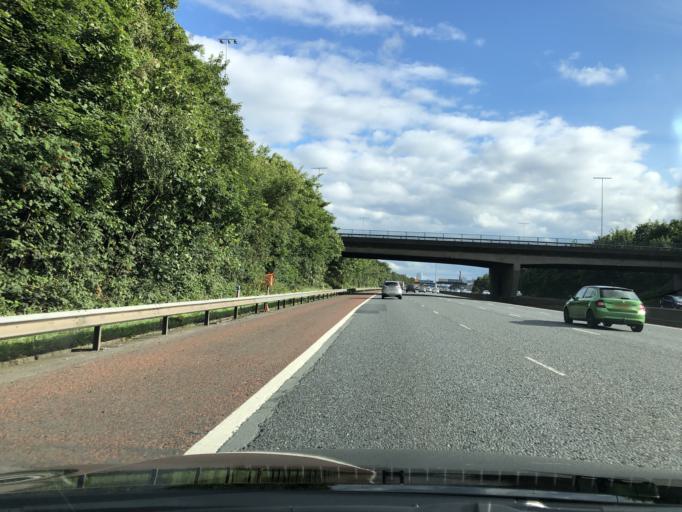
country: GB
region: Northern Ireland
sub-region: Newtownabbey District
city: Newtownabbey
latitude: 54.6301
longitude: -5.9189
